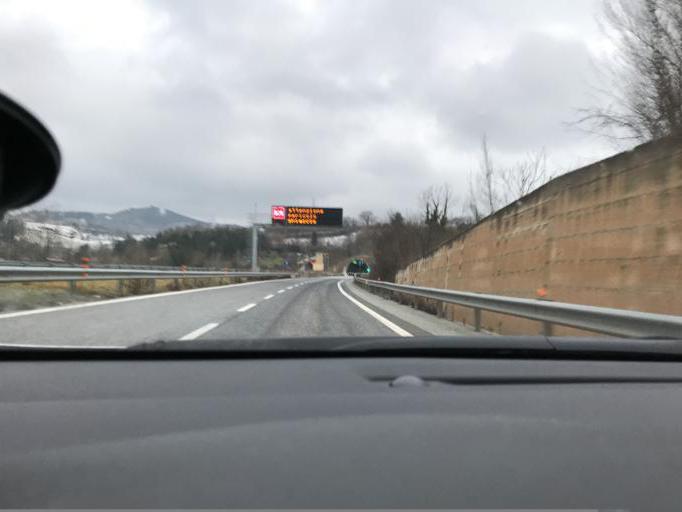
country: IT
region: The Marches
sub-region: Provincia di Ancona
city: Fabriano
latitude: 43.3269
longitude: 12.9205
